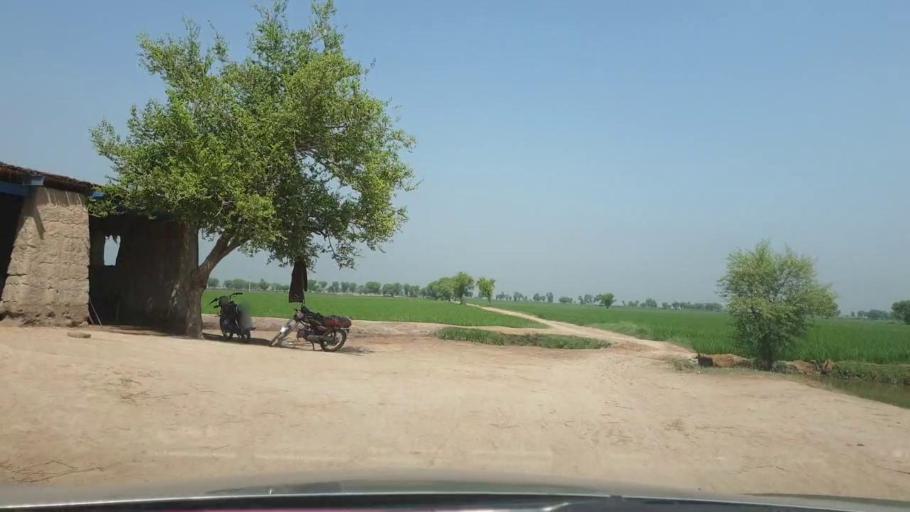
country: PK
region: Sindh
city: Kambar
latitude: 27.5946
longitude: 67.9068
